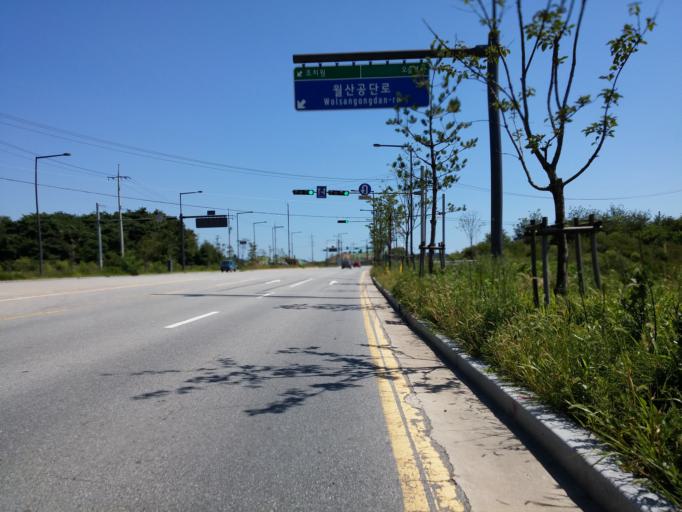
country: KR
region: Daejeon
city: Songgang-dong
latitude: 36.5344
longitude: 127.2794
